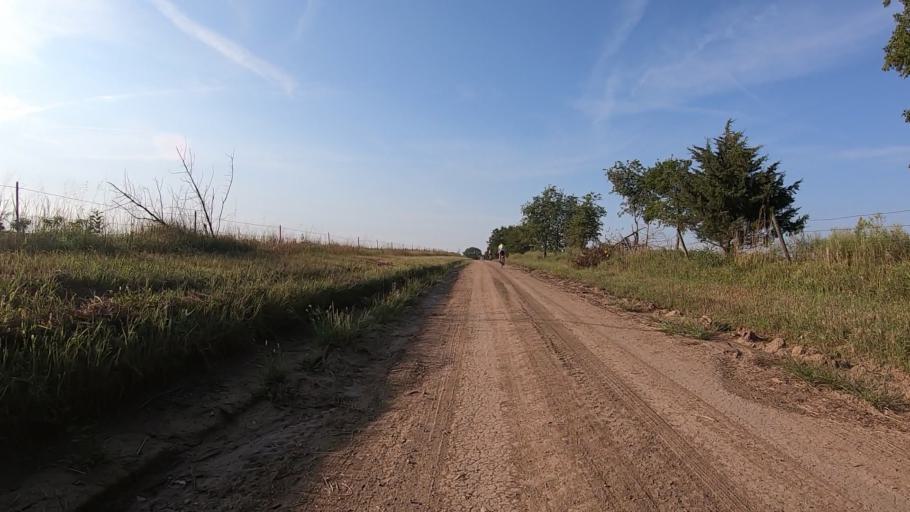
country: US
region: Kansas
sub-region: Marshall County
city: Blue Rapids
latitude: 39.7143
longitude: -96.8067
